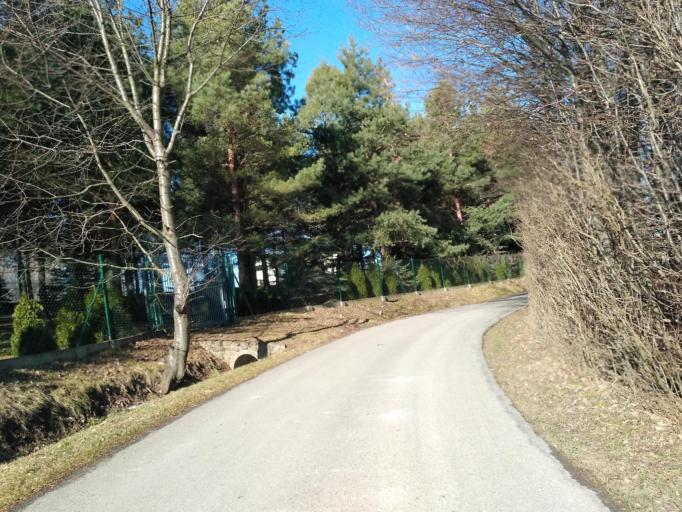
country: PL
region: Subcarpathian Voivodeship
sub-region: Powiat rzeszowski
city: Siedliska
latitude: 49.9384
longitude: 21.9463
